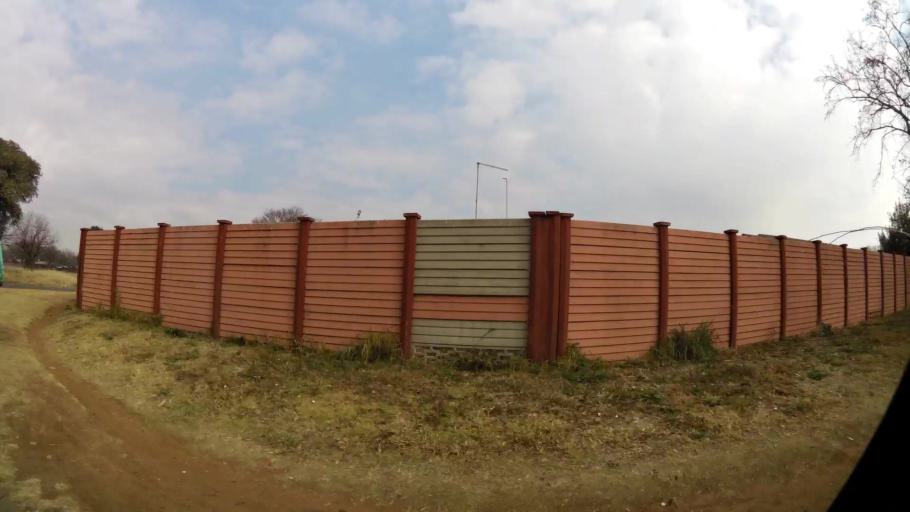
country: ZA
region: Gauteng
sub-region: Sedibeng District Municipality
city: Vanderbijlpark
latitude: -26.6805
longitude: 27.8340
